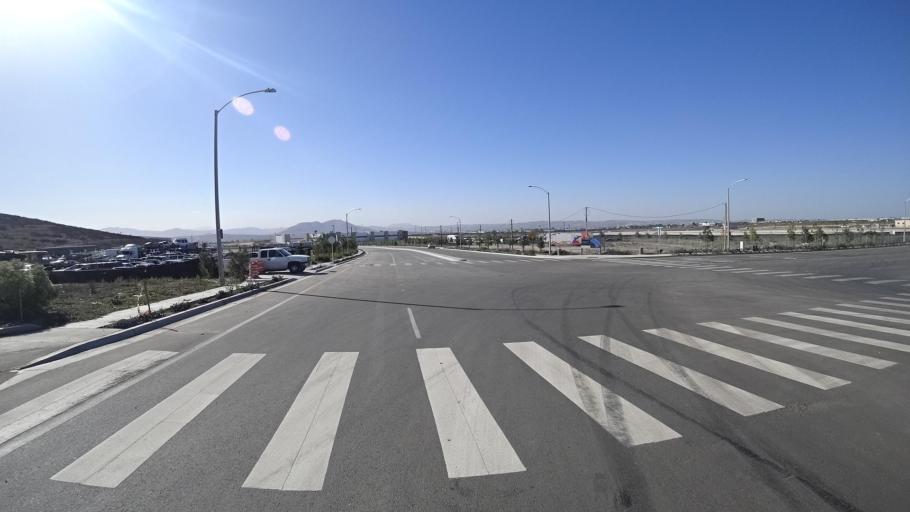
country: MX
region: Baja California
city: Tijuana
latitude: 32.5675
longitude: -116.9127
